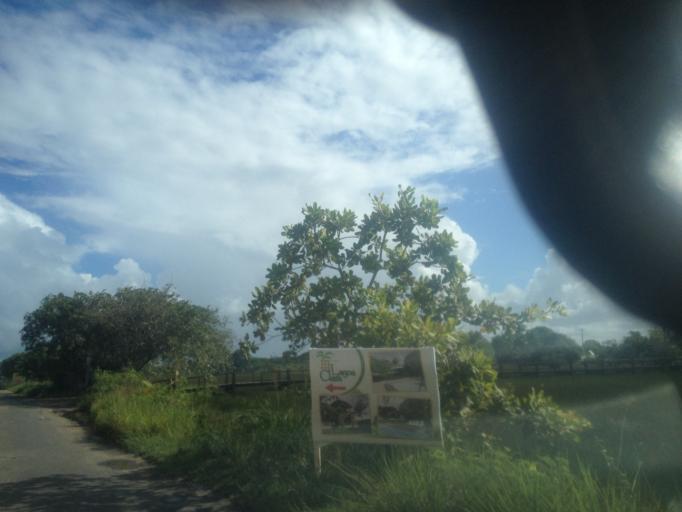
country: BR
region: Bahia
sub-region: Mata De Sao Joao
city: Mata de Sao Joao
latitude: -12.6198
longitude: -38.0465
